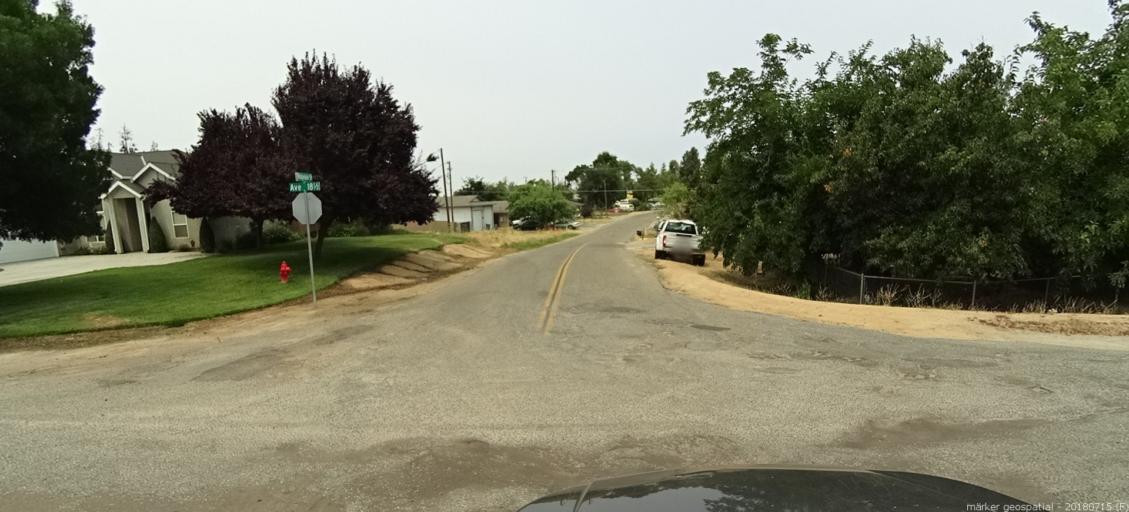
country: US
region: California
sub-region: Madera County
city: Madera Acres
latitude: 37.0181
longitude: -120.0818
